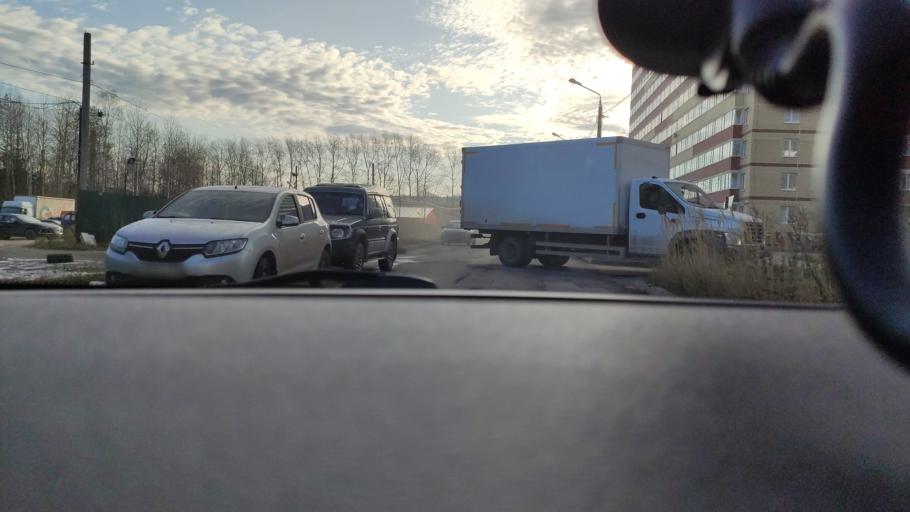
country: RU
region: Perm
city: Kondratovo
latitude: 58.0517
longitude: 56.0887
